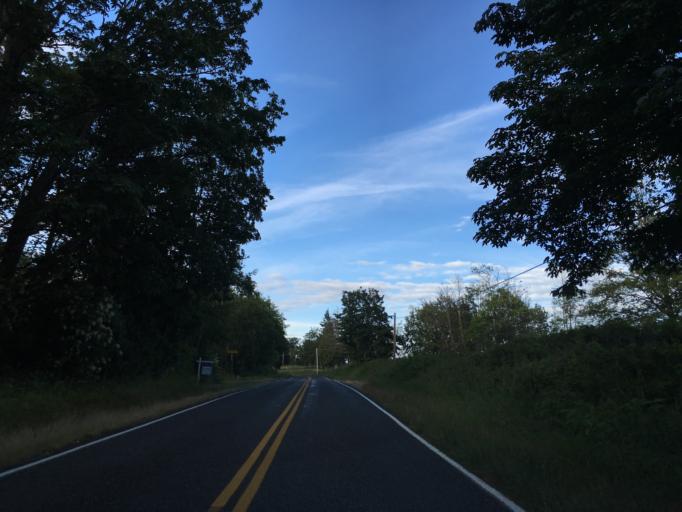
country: CA
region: British Columbia
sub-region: Greater Vancouver Regional District
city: White Rock
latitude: 48.9580
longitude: -122.8097
